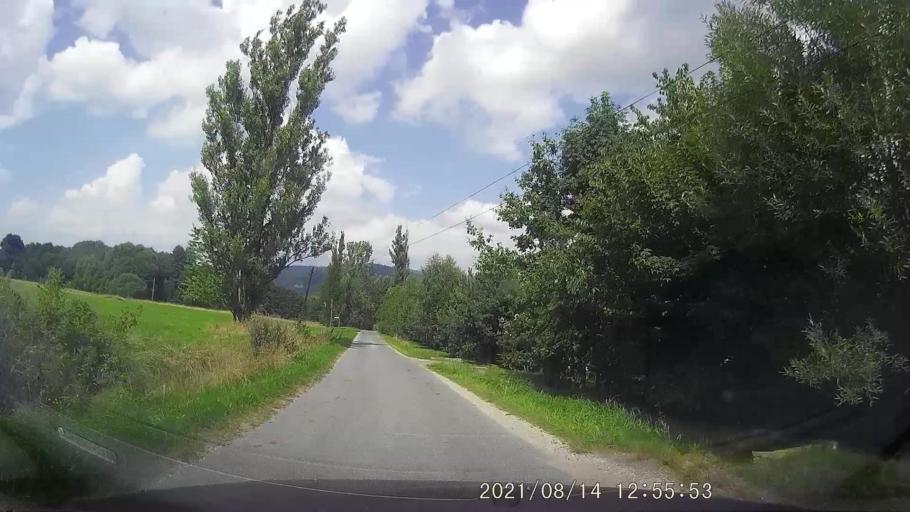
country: PL
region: Lower Silesian Voivodeship
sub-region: Powiat klodzki
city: Ladek-Zdroj
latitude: 50.3332
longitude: 16.8342
